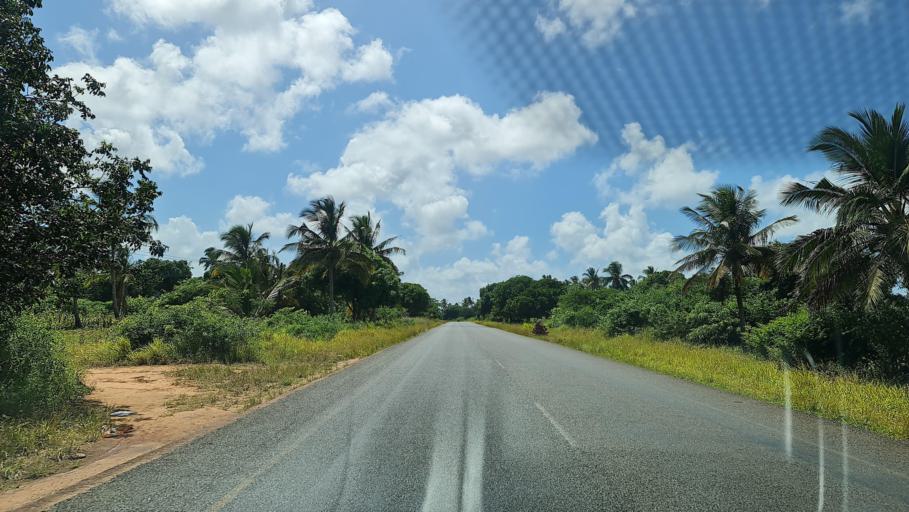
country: MZ
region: Inhambane
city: Maxixe
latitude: -24.5402
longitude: 34.9294
